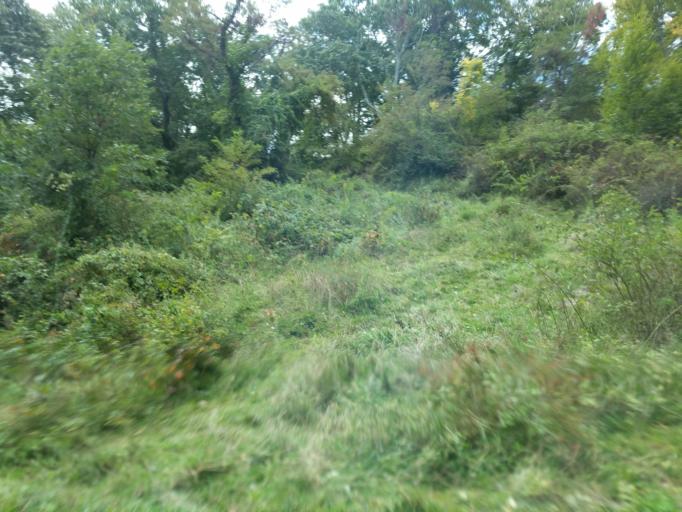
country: US
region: North Carolina
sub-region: Haywood County
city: Clyde
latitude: 35.5635
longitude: -82.9108
